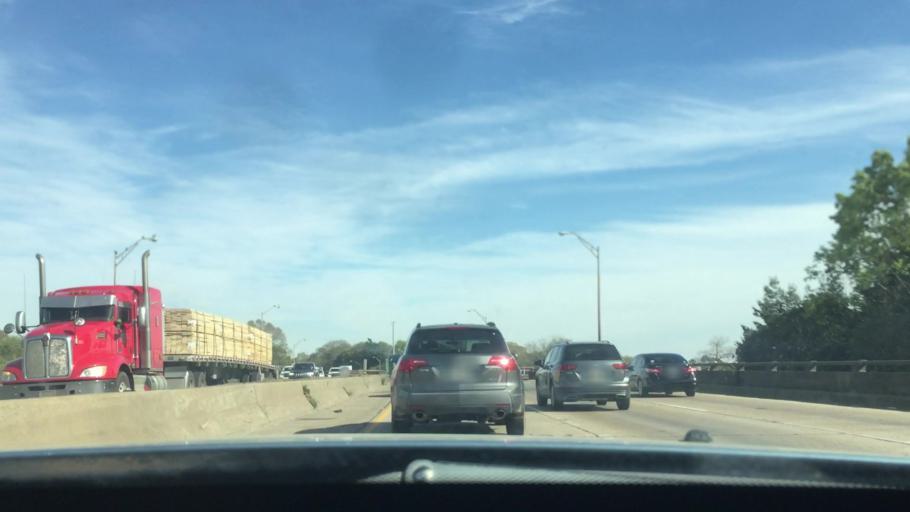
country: US
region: Louisiana
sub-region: East Baton Rouge Parish
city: Baton Rouge
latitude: 30.4273
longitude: -91.1693
